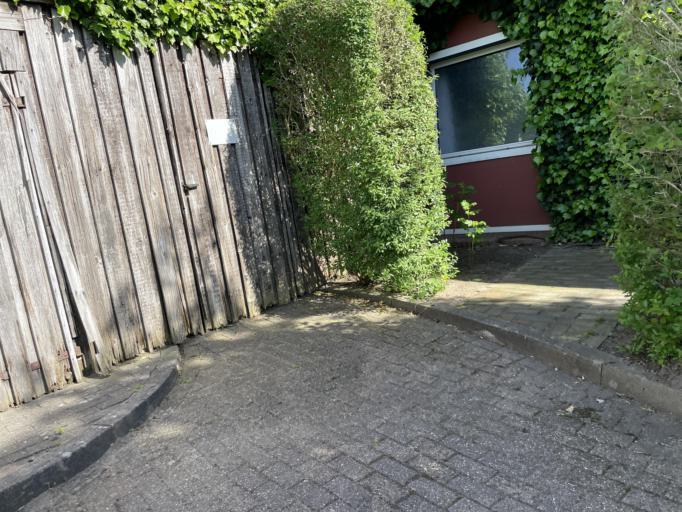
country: DE
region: Schleswig-Holstein
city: Husum
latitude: 54.4728
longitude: 9.0587
